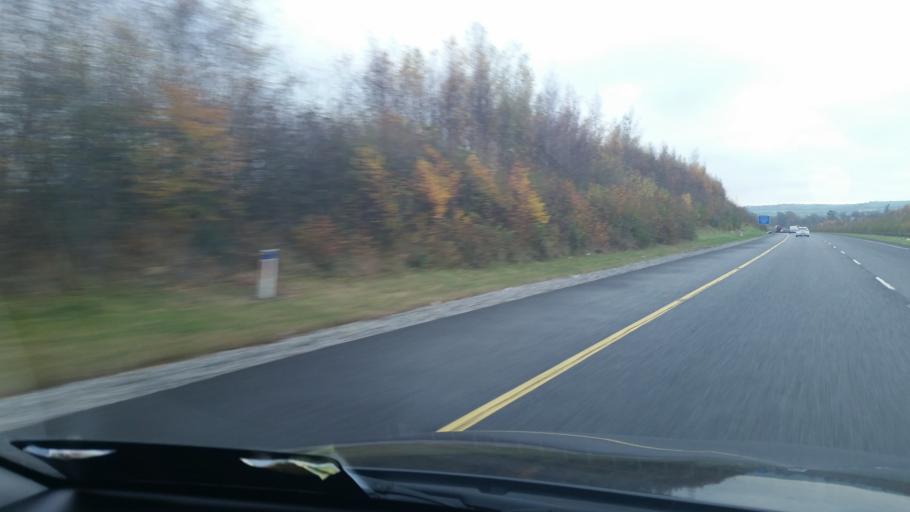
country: IE
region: Leinster
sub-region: Lu
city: Drogheda
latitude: 53.6761
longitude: -6.3551
